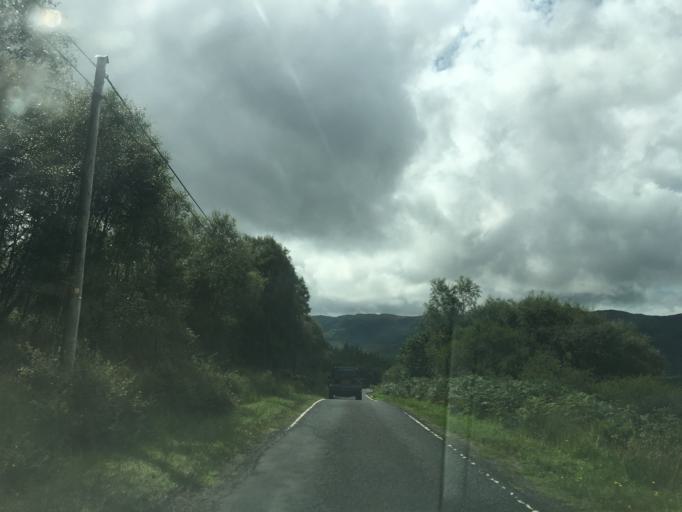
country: GB
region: Scotland
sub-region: Argyll and Bute
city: Port Bannatyne
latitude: 55.9893
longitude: -5.1534
